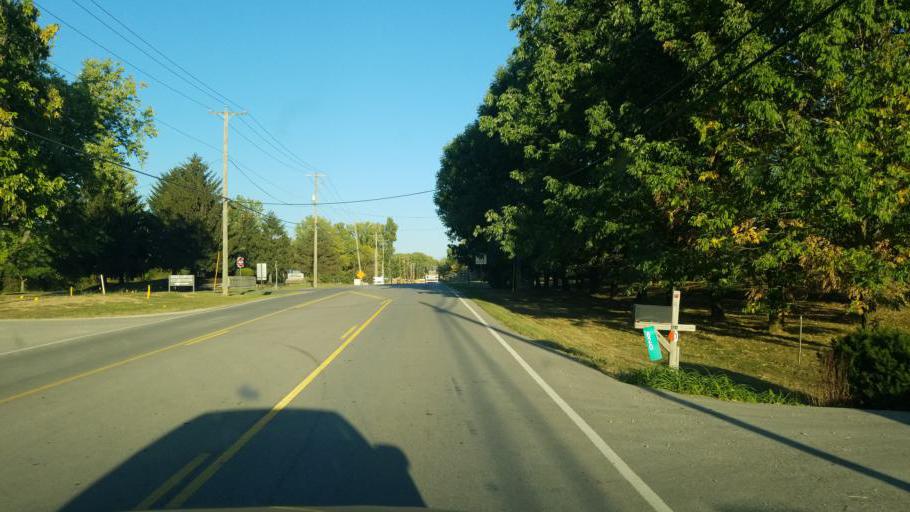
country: US
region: Ohio
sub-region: Delaware County
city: Lewis Center
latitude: 40.2002
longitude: -83.0214
